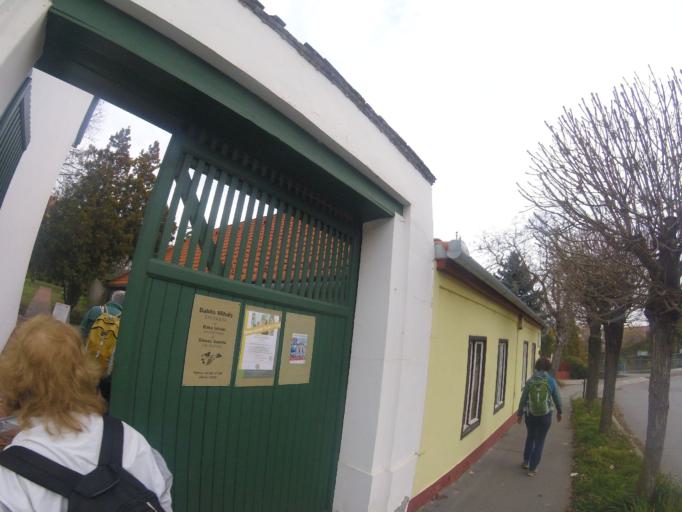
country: HU
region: Tolna
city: Szekszard
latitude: 46.3504
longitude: 18.6957
